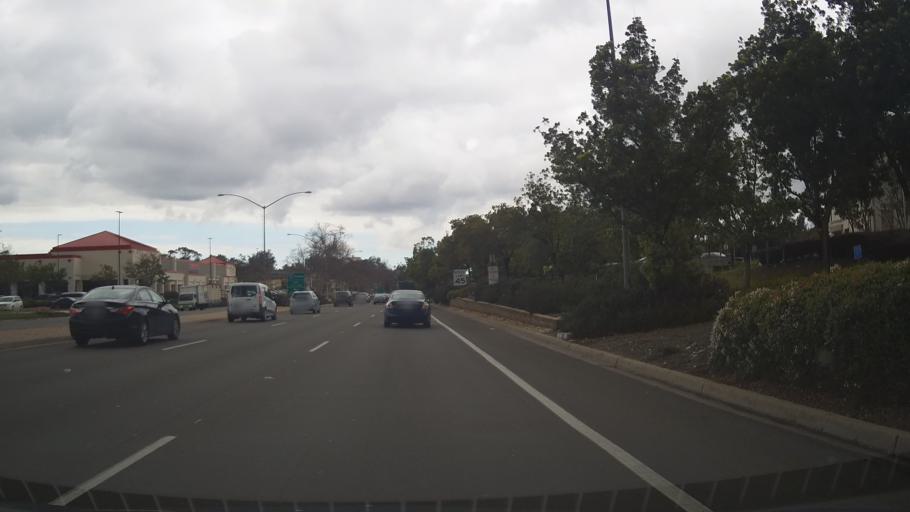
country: US
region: California
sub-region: San Diego County
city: La Mesa
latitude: 32.7753
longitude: -117.0232
